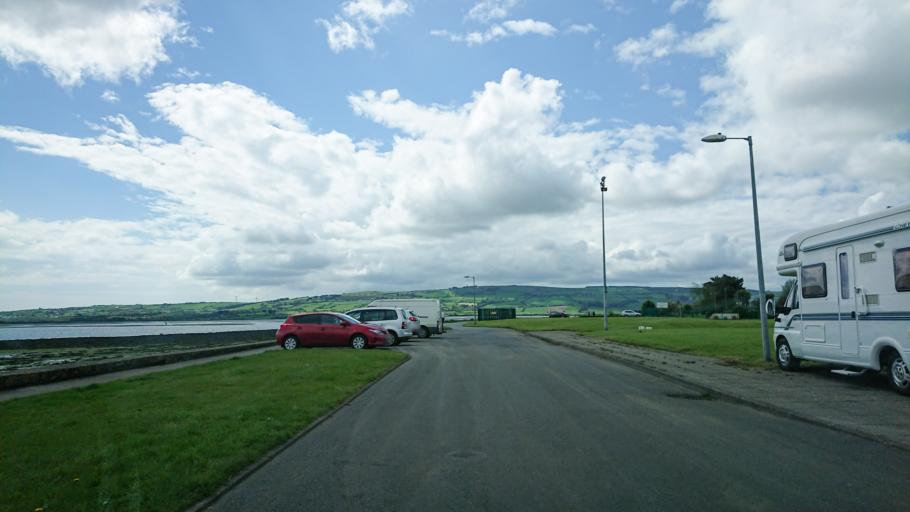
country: IE
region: Munster
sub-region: Waterford
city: Dungarvan
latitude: 52.0854
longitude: -7.6212
